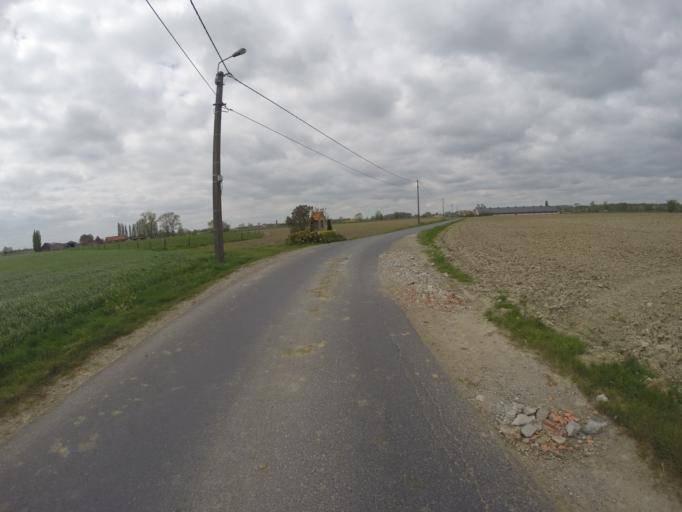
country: BE
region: Flanders
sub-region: Provincie Oost-Vlaanderen
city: Aalter
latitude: 51.0258
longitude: 3.4588
